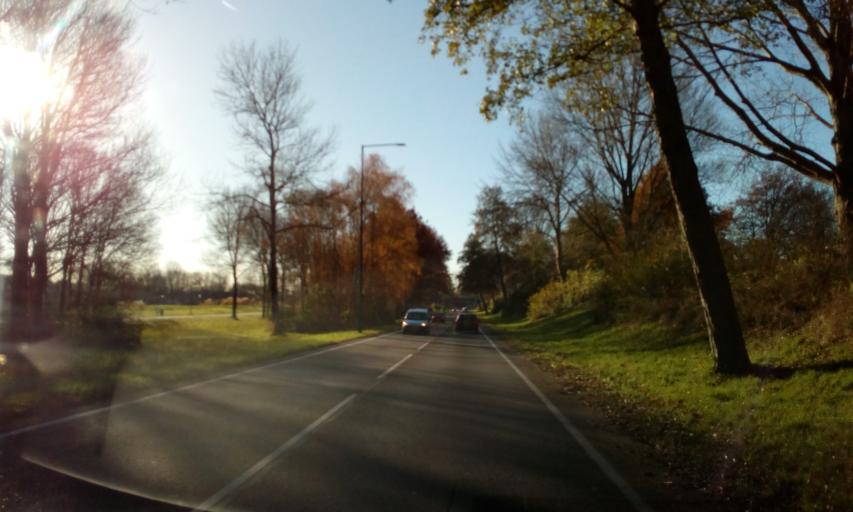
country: NL
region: South Holland
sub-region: Gemeente Zoetermeer
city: Zoetermeer
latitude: 52.0732
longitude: 4.5049
